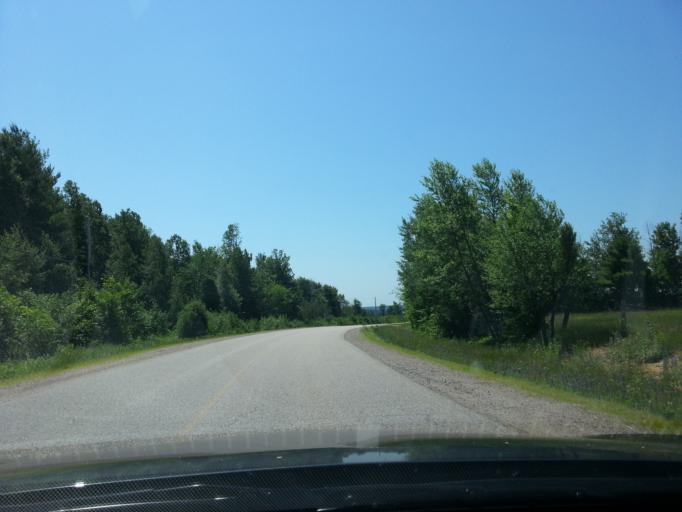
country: CA
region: Ontario
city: Arnprior
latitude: 45.5434
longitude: -76.3652
